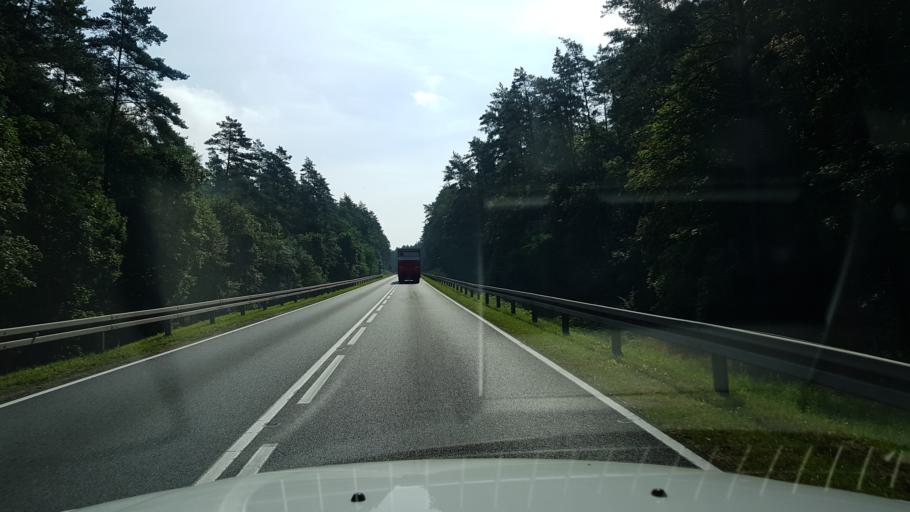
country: PL
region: West Pomeranian Voivodeship
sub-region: Powiat walecki
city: Miroslawiec
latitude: 53.3496
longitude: 16.1664
